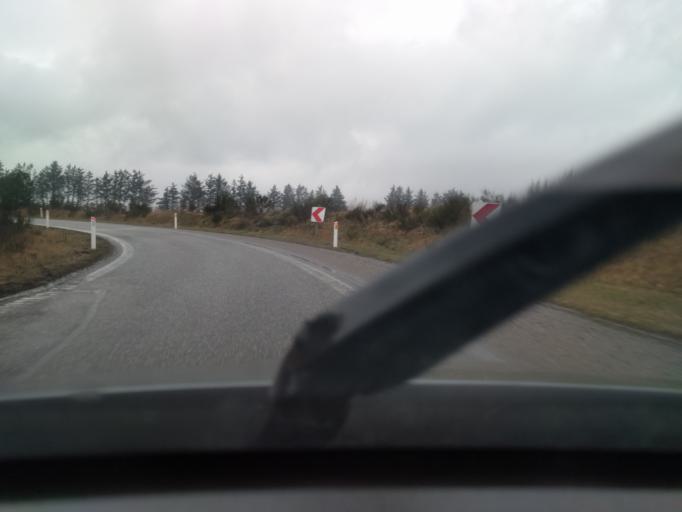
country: DK
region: Central Jutland
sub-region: Viborg Kommune
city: Viborg
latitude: 56.3887
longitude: 9.4493
